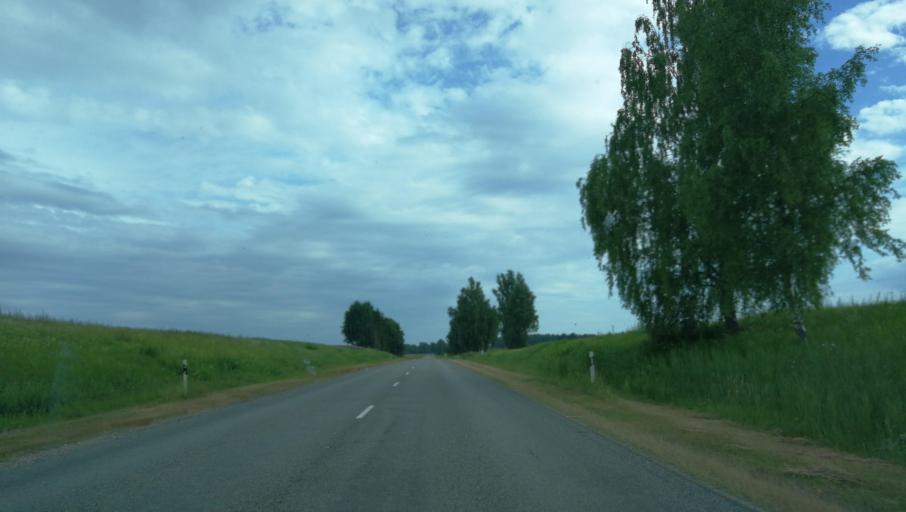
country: LV
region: Valmieras Rajons
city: Valmiera
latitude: 57.6057
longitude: 25.4567
